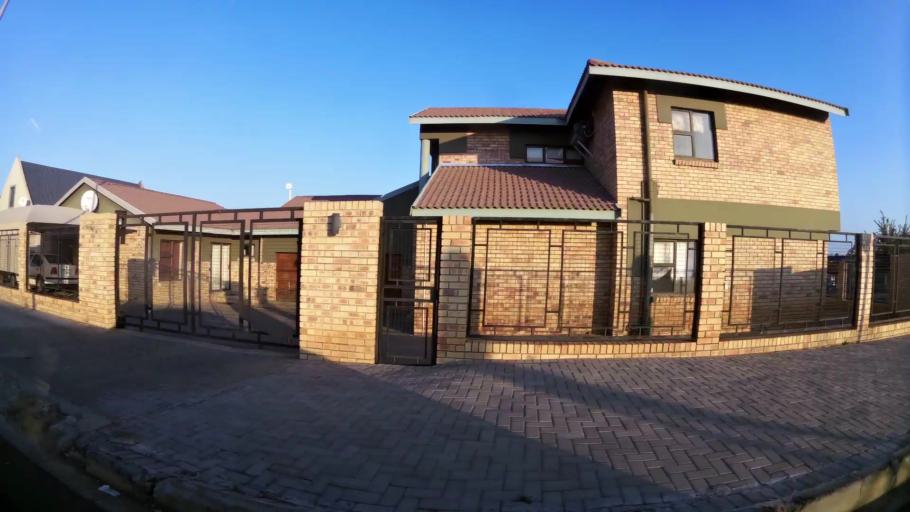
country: ZA
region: Orange Free State
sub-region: Mangaung Metropolitan Municipality
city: Bloemfontein
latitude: -29.0951
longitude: 26.1656
